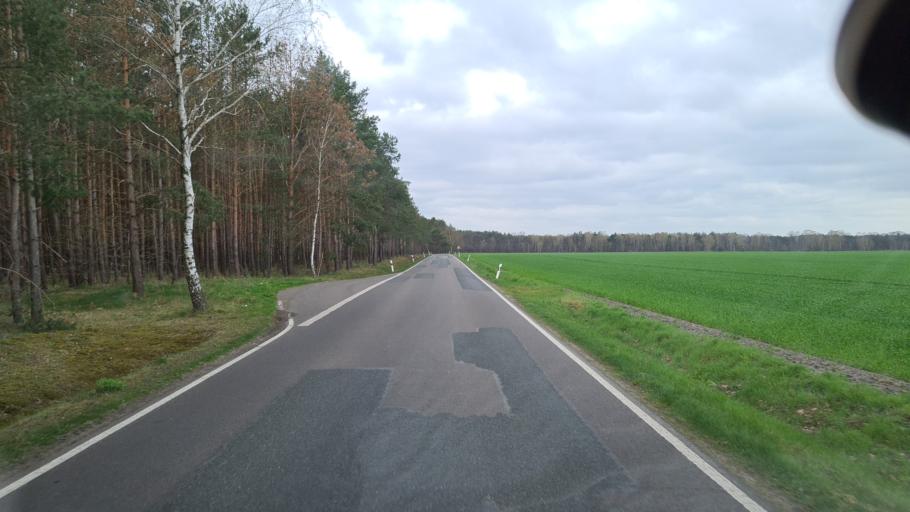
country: DE
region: Brandenburg
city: Hohenbocka
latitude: 51.4538
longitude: 13.9834
